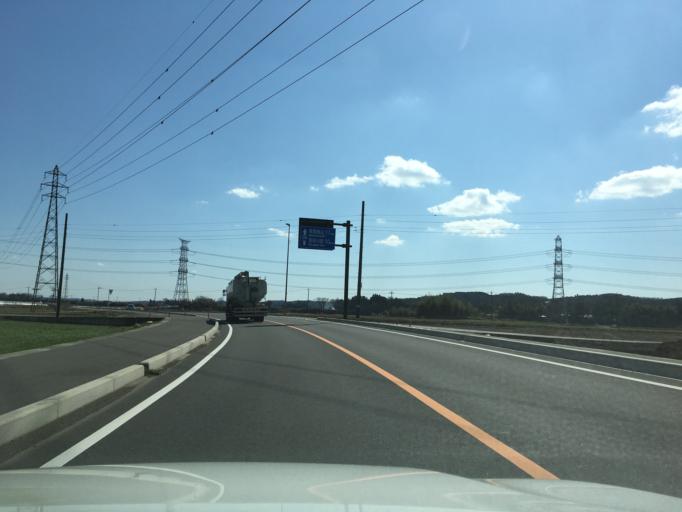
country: JP
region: Tochigi
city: Otawara
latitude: 36.7917
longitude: 140.1151
